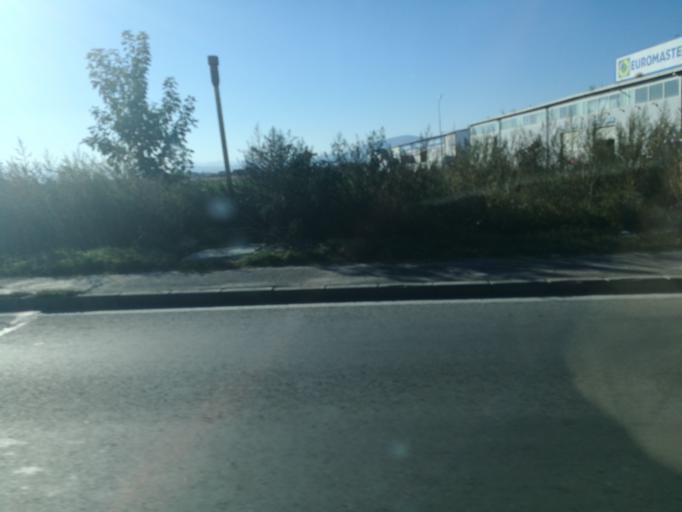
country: RO
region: Brasov
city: Brasov
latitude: 45.6881
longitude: 25.5829
